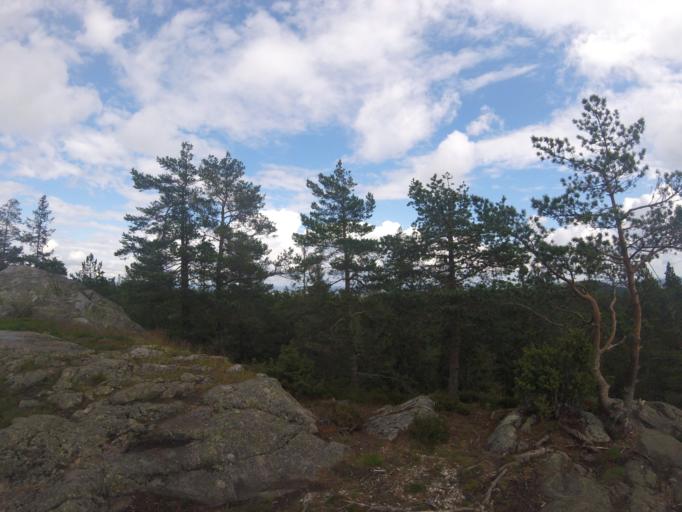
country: NO
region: Akershus
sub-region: Raelingen
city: Fjerdingby
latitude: 59.9036
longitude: 11.0407
